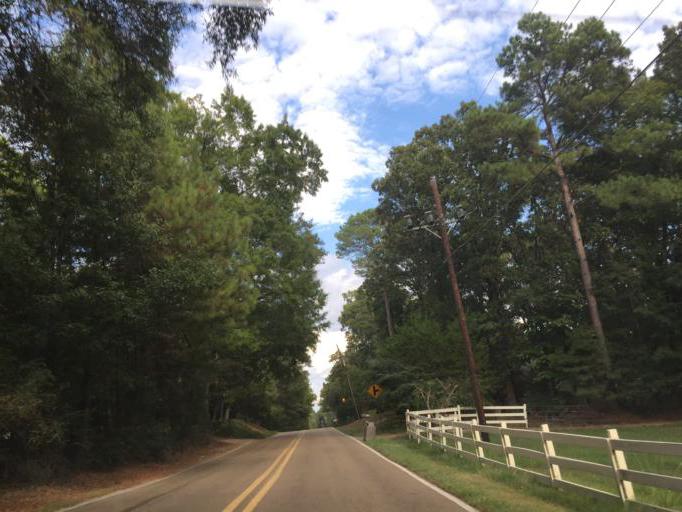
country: US
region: Mississippi
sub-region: Madison County
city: Madison
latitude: 32.4651
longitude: -90.0702
